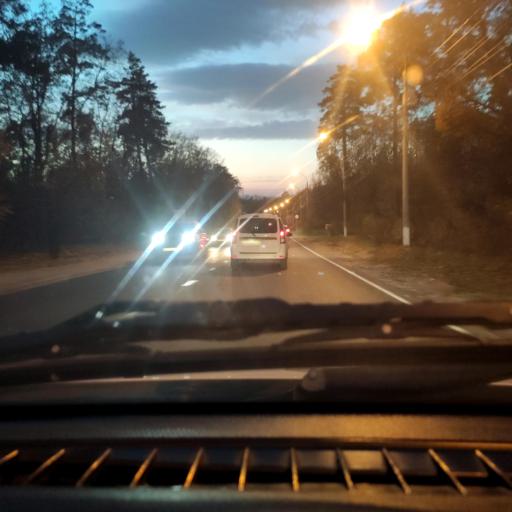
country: RU
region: Samara
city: Tol'yatti
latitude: 53.4929
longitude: 49.2978
